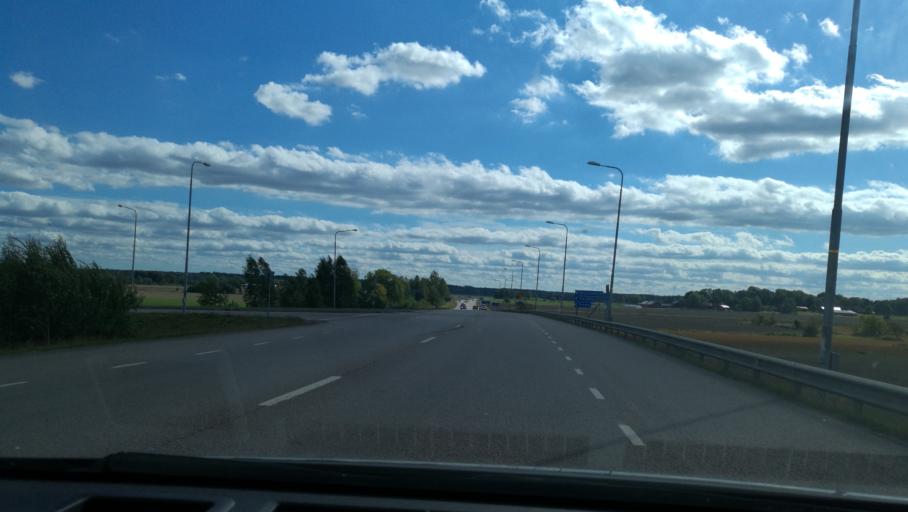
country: SE
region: Vaestra Goetaland
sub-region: Mariestads Kommun
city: Mariestad
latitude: 58.6746
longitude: 13.8166
